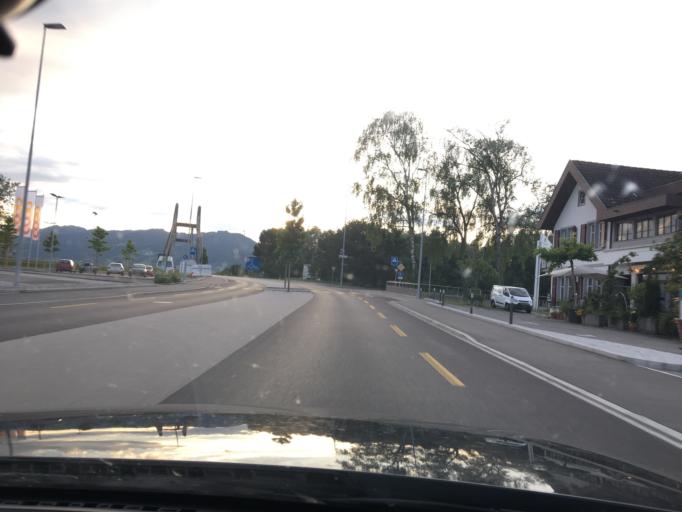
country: CH
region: Saint Gallen
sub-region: Wahlkreis Rheintal
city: Diepoldsau
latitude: 47.3896
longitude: 9.6501
